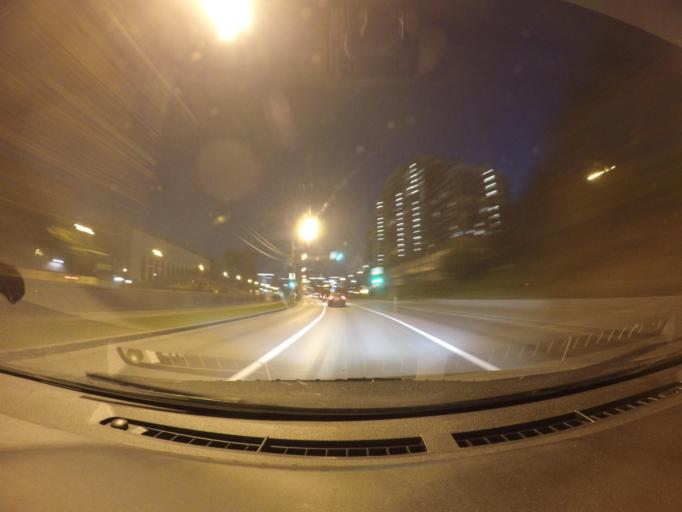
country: RU
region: Moscow
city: Lefortovo
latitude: 55.7868
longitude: 37.6983
